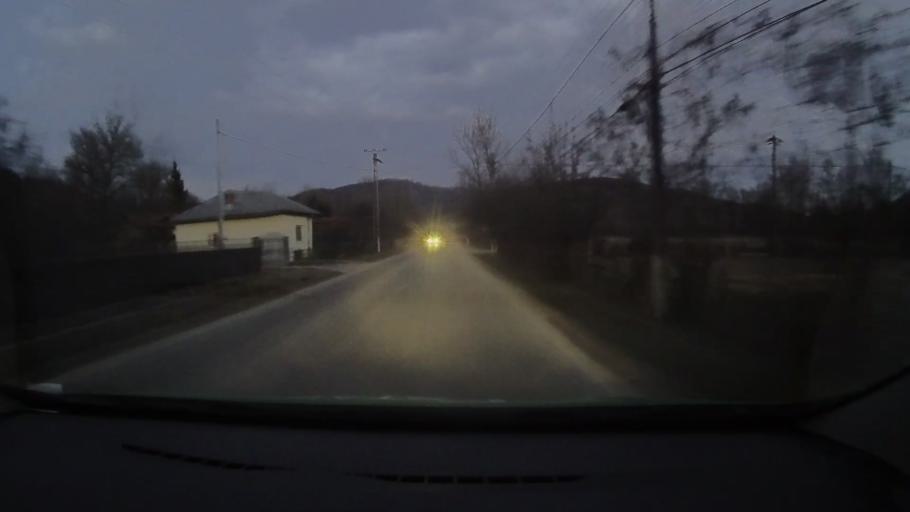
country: RO
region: Prahova
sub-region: Comuna Provita de Jos
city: Provita de Jos
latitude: 45.1204
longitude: 25.6623
